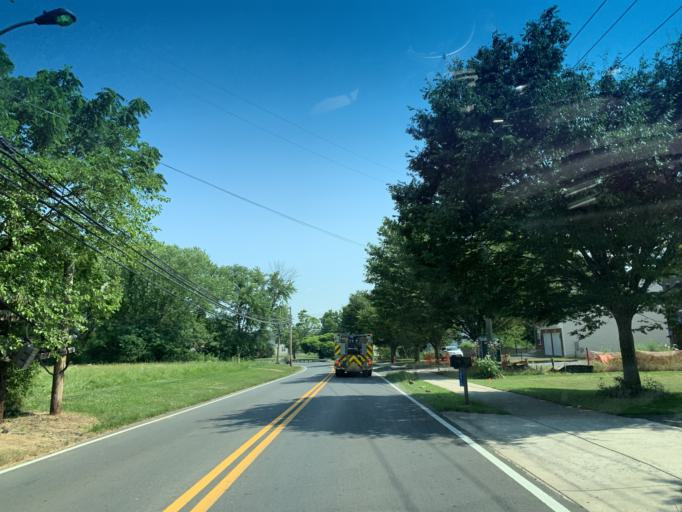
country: US
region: Maryland
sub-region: Montgomery County
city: Poolesville
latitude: 39.1394
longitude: -77.4071
